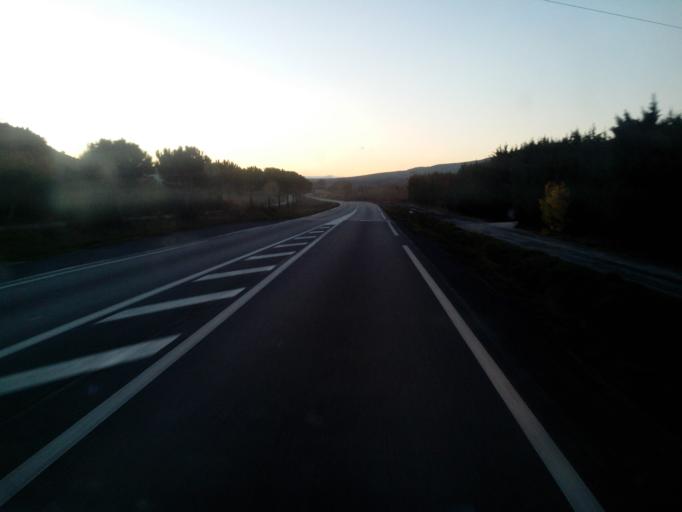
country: FR
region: Languedoc-Roussillon
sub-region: Departement des Pyrenees-Orientales
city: Baixas
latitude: 42.7779
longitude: 2.8252
